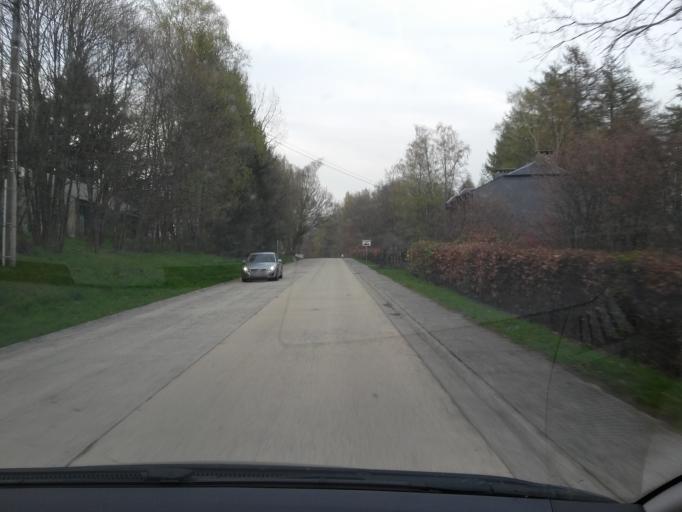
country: BE
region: Wallonia
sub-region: Province du Luxembourg
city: Herbeumont
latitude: 49.7866
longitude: 5.2513
